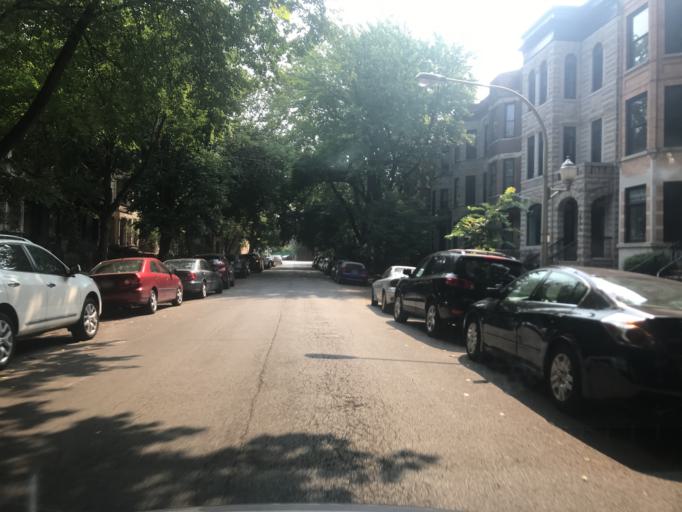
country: US
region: Illinois
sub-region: Cook County
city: Chicago
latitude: 41.9440
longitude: -87.6516
